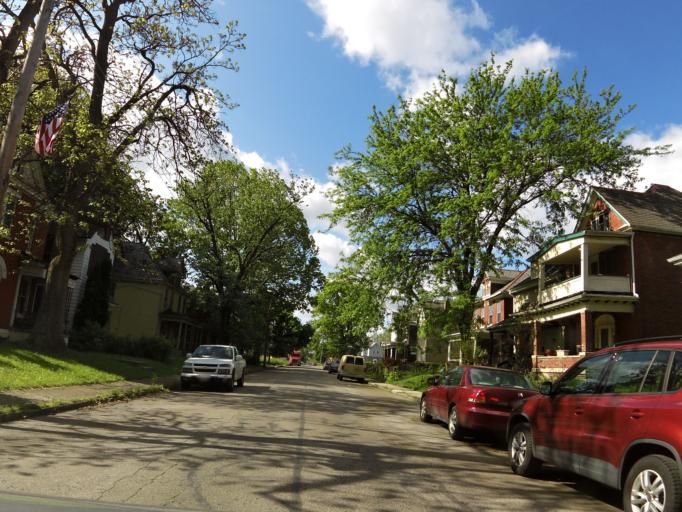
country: US
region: Ohio
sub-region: Franklin County
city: Columbus
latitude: 39.9511
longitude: -82.9687
